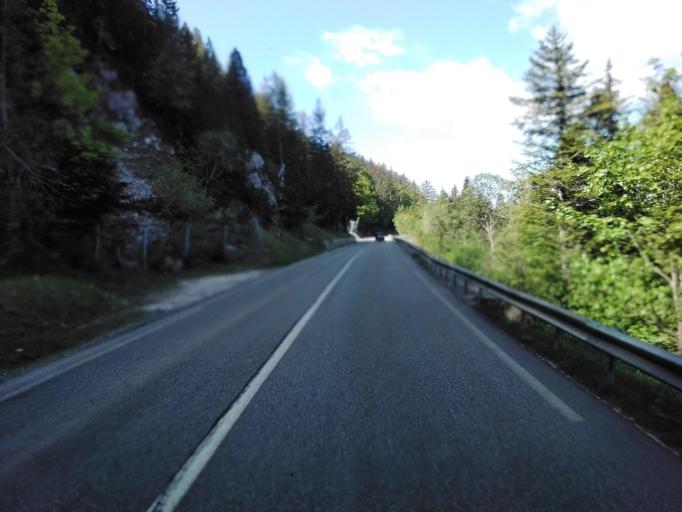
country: FR
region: Rhone-Alpes
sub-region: Departement de l'Ain
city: Gex
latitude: 46.3793
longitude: 6.0432
